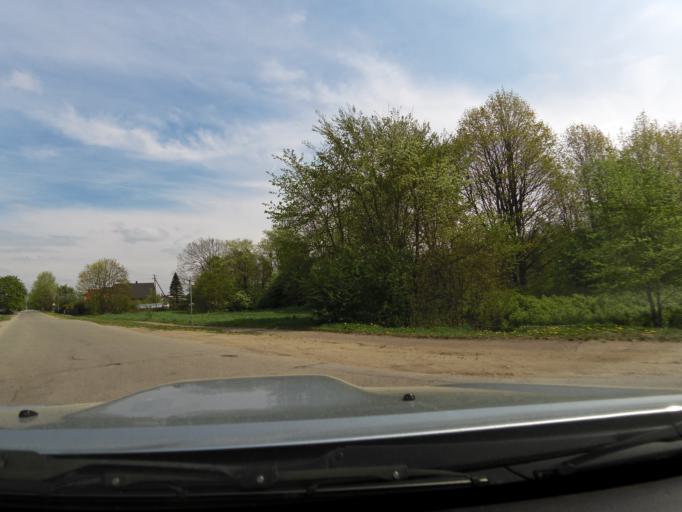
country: LT
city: Salcininkai
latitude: 54.4354
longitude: 25.3000
